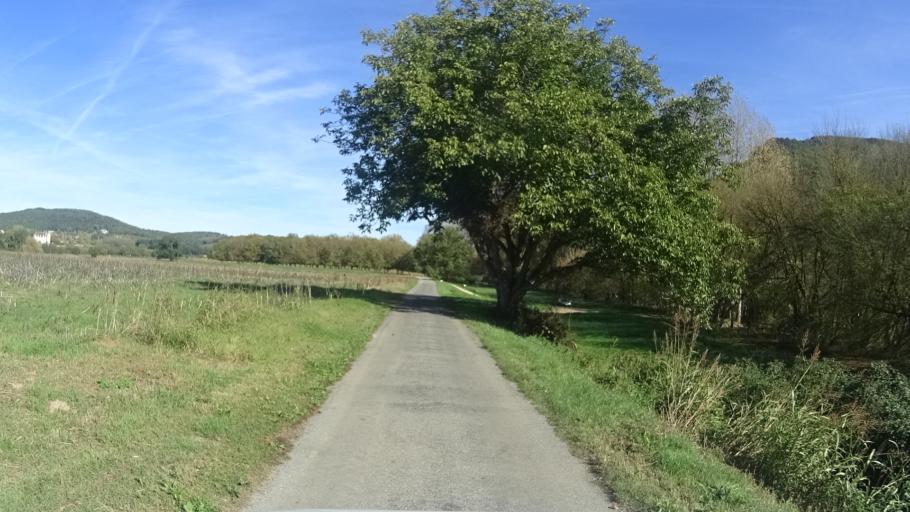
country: FR
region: Aquitaine
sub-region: Departement de la Dordogne
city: Saint-Cyprien
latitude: 44.8287
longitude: 1.1147
